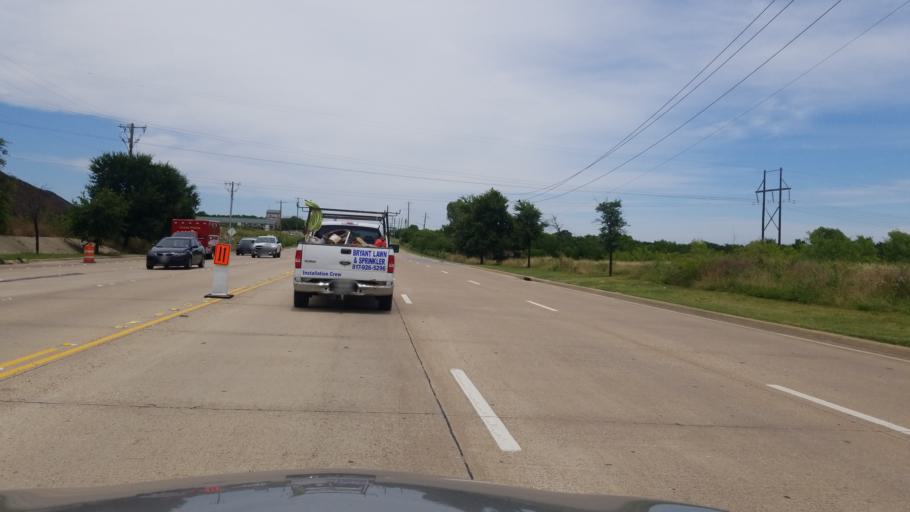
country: US
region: Texas
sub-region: Dallas County
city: Grand Prairie
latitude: 32.6746
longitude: -96.9851
